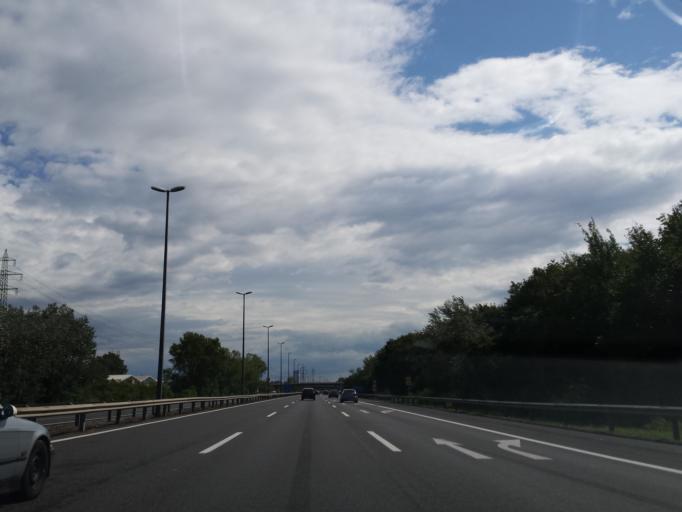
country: AT
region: Lower Austria
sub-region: Politischer Bezirk Korneuburg
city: Langenzersdorf
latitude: 48.2855
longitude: 16.3615
